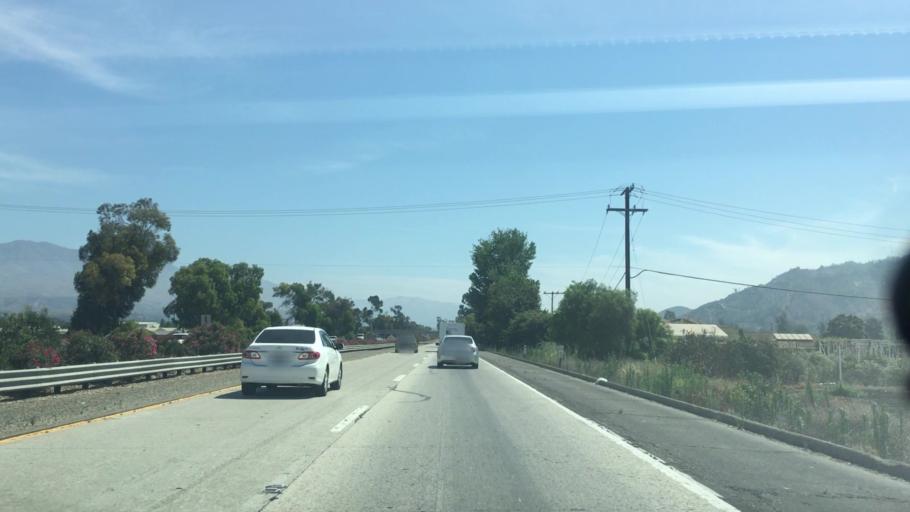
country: US
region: California
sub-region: Ventura County
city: Saticoy
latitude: 34.3187
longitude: -119.1073
